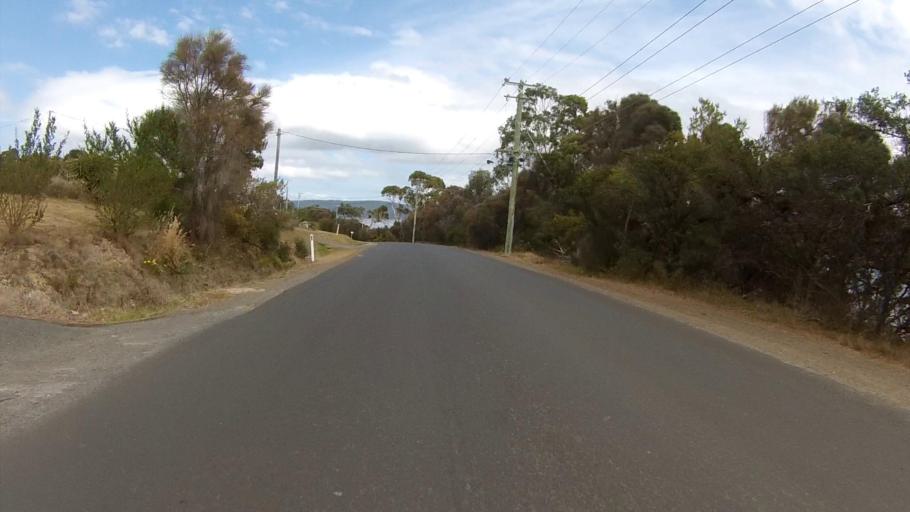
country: AU
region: Tasmania
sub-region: Kingborough
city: Margate
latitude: -43.0244
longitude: 147.2909
